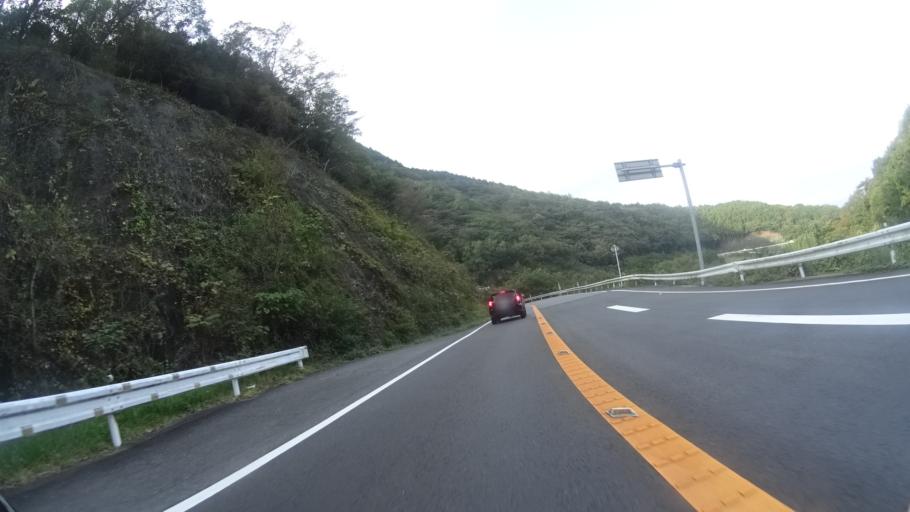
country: JP
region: Oita
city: Beppu
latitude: 33.2803
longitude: 131.4516
